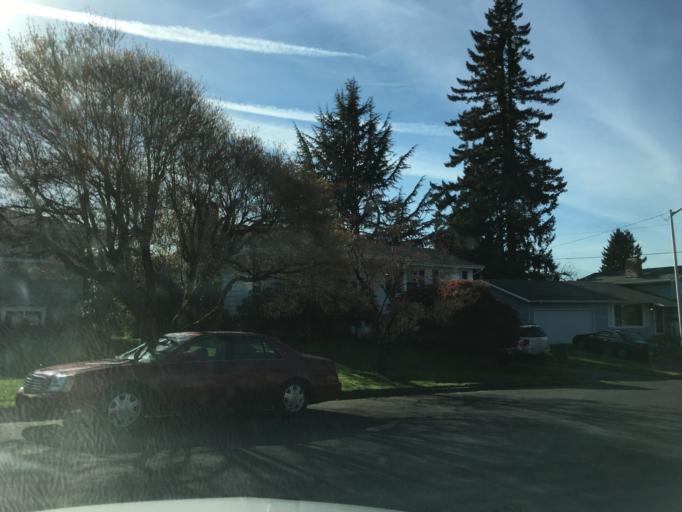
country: US
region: Oregon
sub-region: Multnomah County
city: Lents
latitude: 45.5474
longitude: -122.5255
